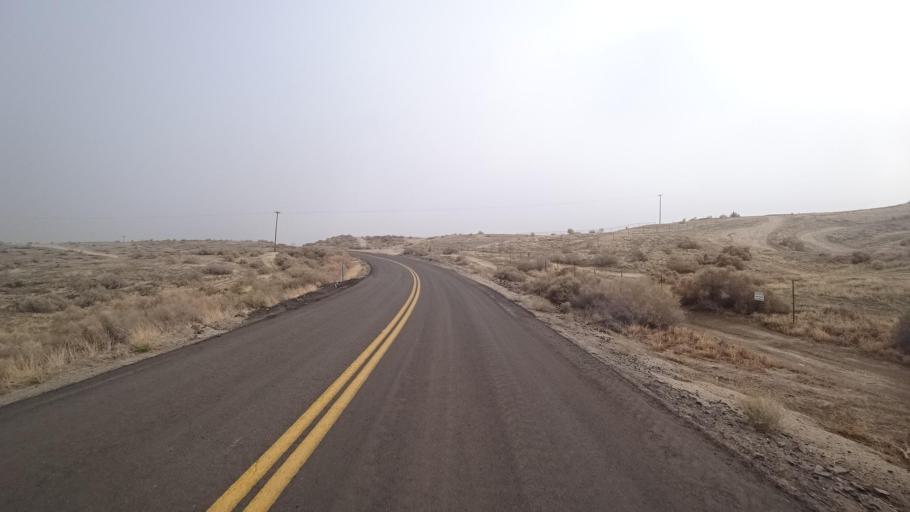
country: US
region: California
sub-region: Kern County
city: Ford City
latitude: 35.1641
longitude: -119.3878
